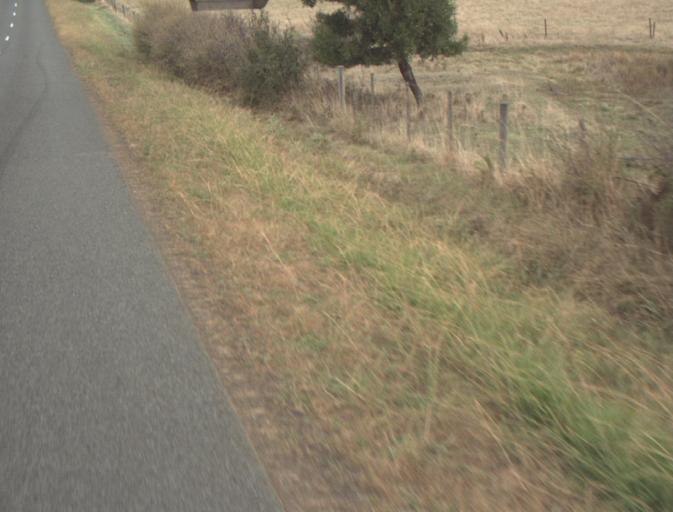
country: AU
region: Tasmania
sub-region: Northern Midlands
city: Evandale
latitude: -41.5118
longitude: 147.2116
